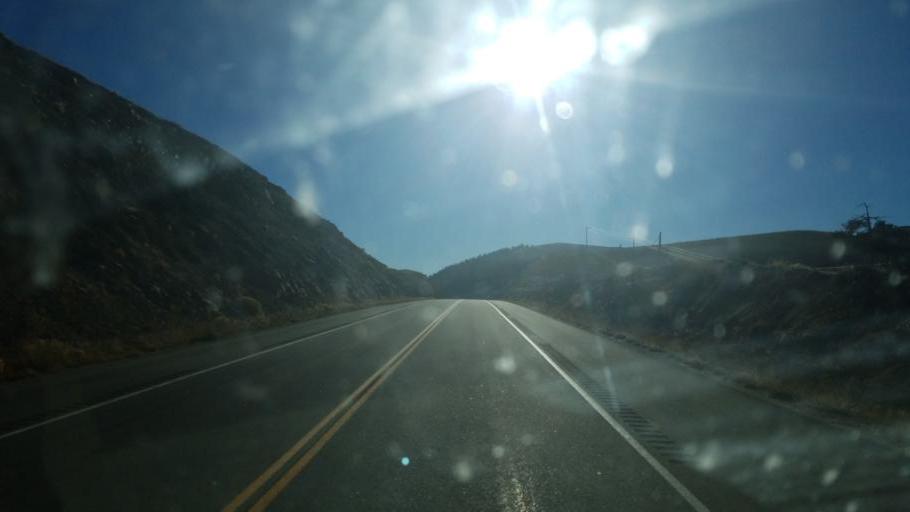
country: US
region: Colorado
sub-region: Gunnison County
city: Gunnison
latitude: 38.5279
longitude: -106.8173
